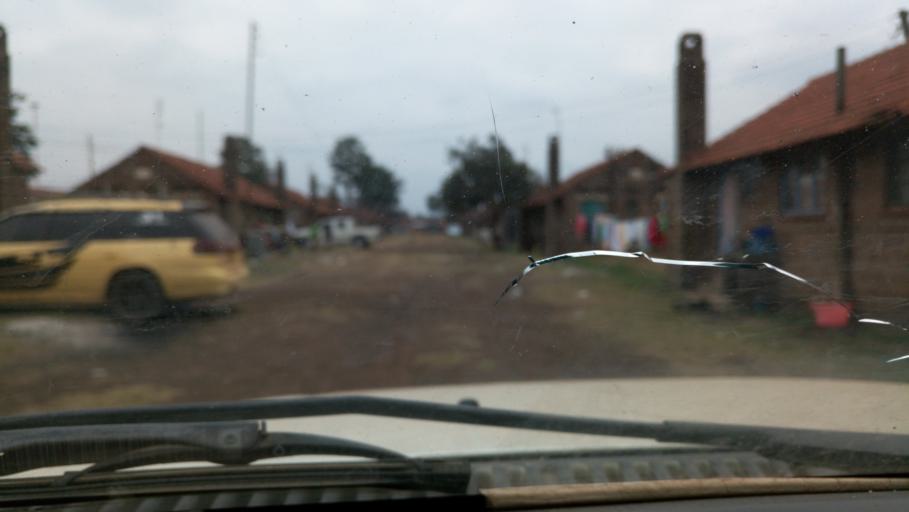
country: KE
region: Nairobi Area
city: Pumwani
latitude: -1.2966
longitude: 36.8540
